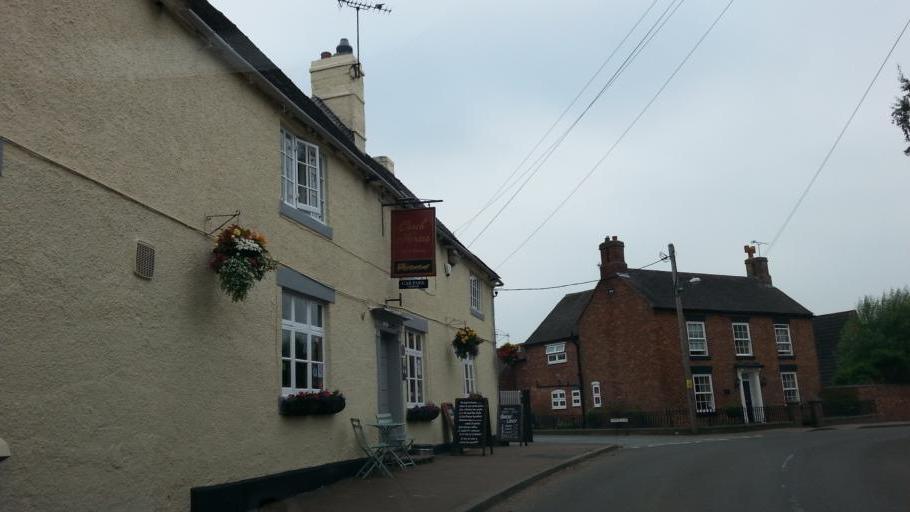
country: GB
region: England
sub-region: Staffordshire
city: Armitage
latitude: 52.8174
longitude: -1.8776
